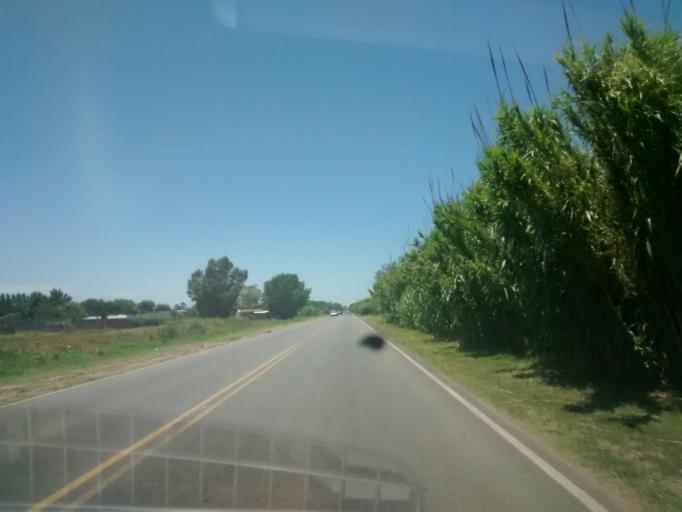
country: AR
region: Buenos Aires
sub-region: Partido de Berisso
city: Berisso
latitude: -34.8851
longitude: -57.8576
